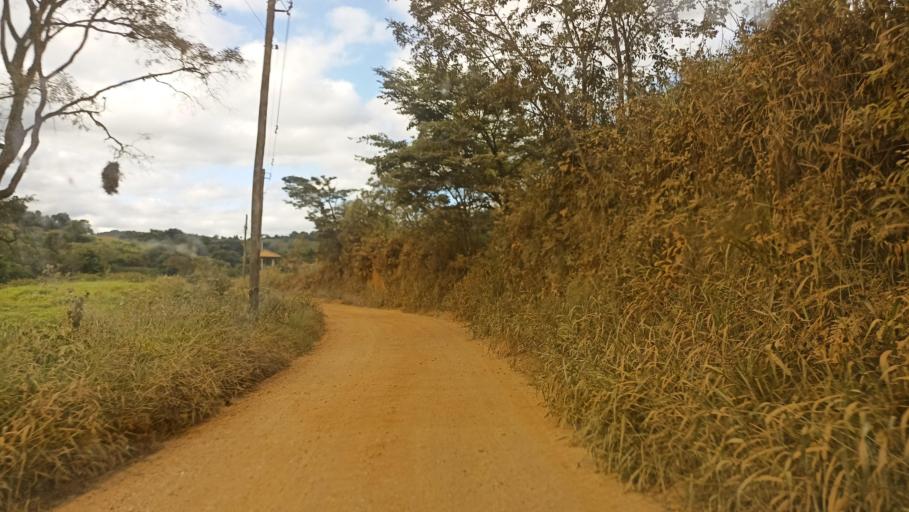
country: BR
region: Minas Gerais
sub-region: Tiradentes
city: Tiradentes
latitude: -21.0975
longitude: -44.0765
